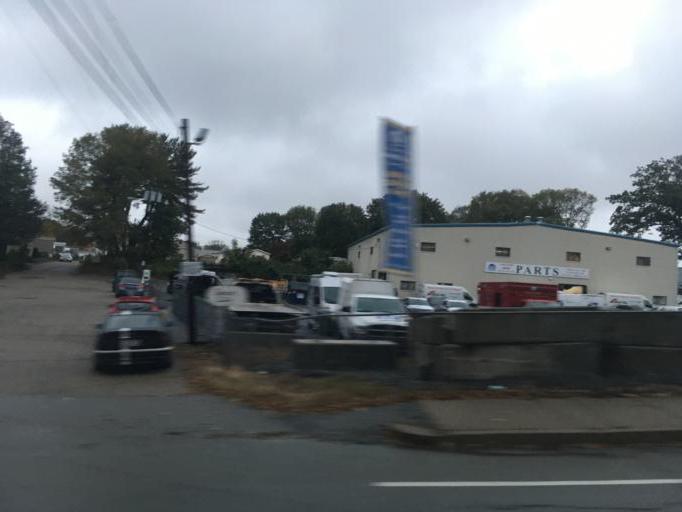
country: US
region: Rhode Island
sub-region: Kent County
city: West Warwick
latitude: 41.7102
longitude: -71.4925
